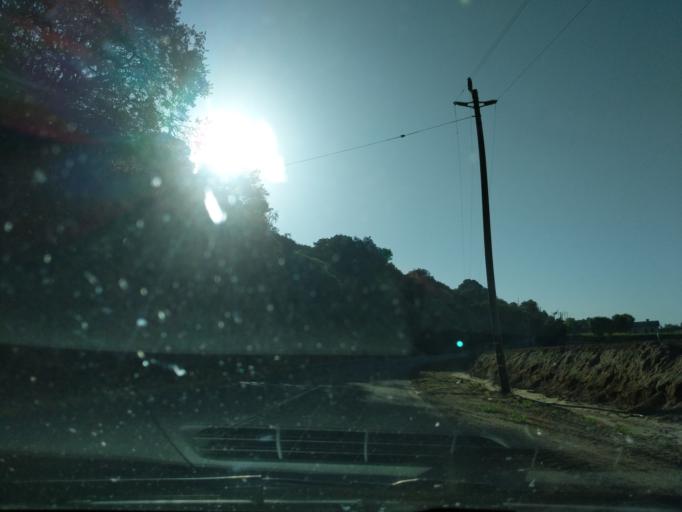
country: US
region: California
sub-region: Monterey County
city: Gonzales
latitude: 36.4781
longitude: -121.4824
